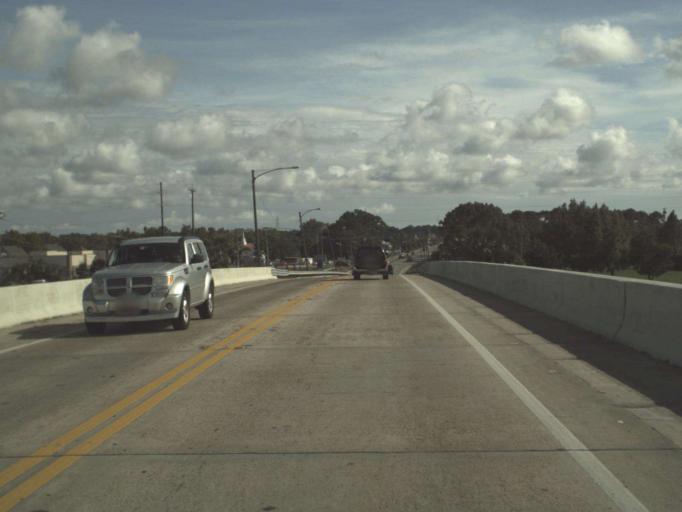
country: US
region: Florida
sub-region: Gulf County
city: Port Saint Joe
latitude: 29.8233
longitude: -85.3083
